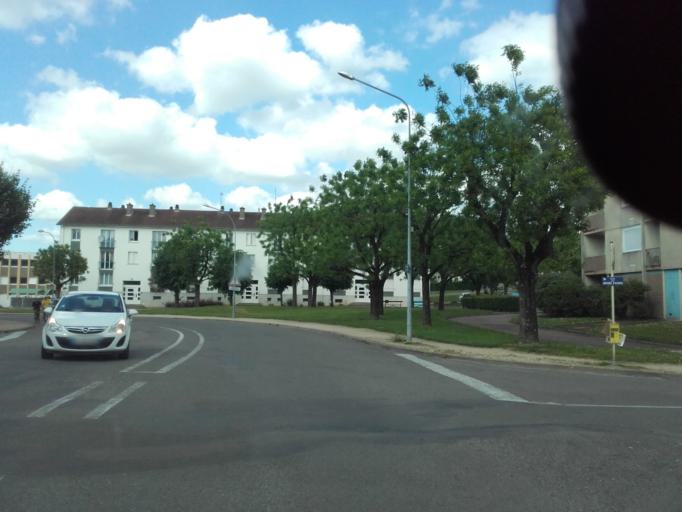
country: FR
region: Bourgogne
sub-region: Departement de Saone-et-Loire
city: Chagny
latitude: 46.9108
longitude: 4.7549
